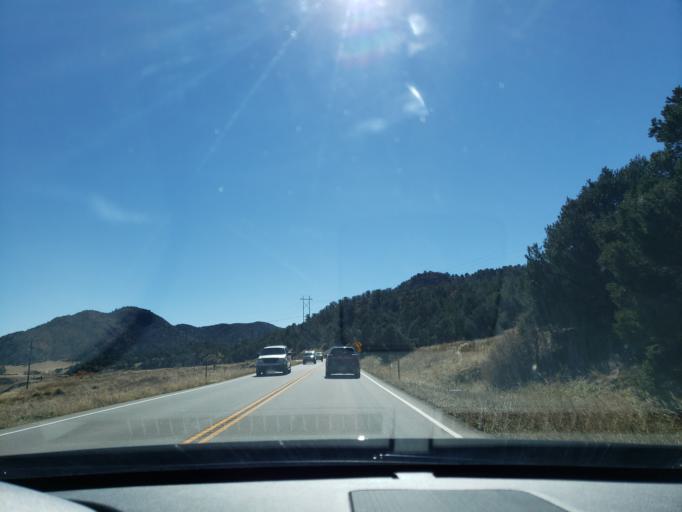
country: US
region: Colorado
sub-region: Fremont County
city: Canon City
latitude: 38.5922
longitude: -105.4245
